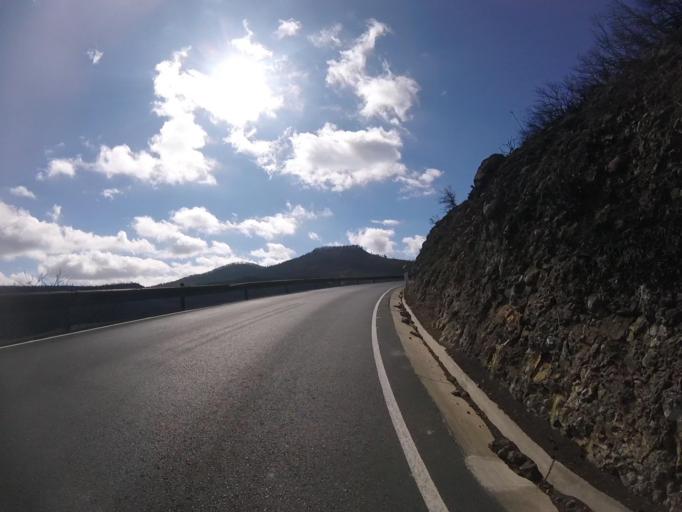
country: ES
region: Canary Islands
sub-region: Provincia de Las Palmas
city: Tejeda
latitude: 27.9912
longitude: -15.5920
